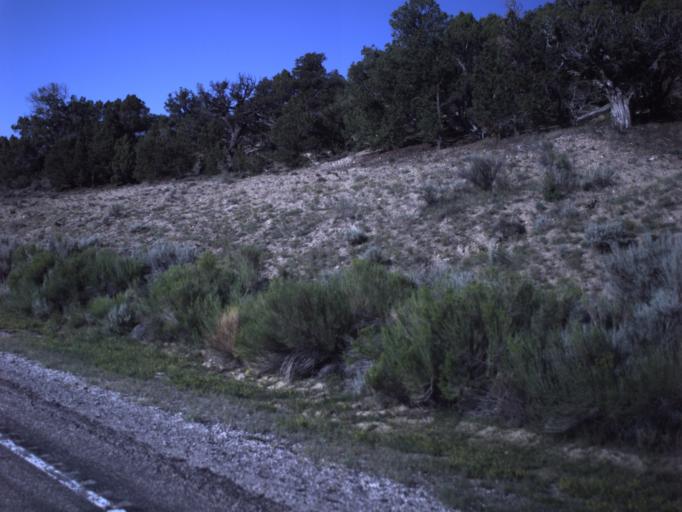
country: US
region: Utah
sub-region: Wayne County
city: Loa
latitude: 38.6545
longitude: -111.4340
